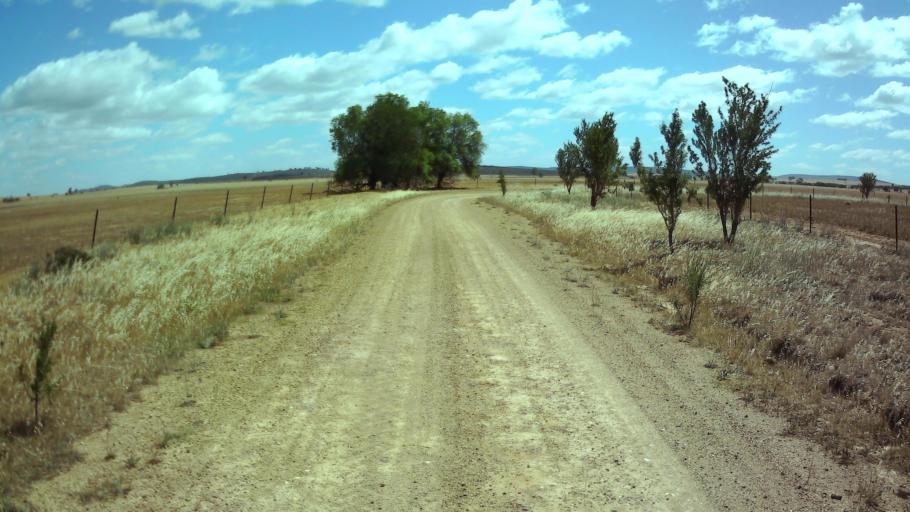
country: AU
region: New South Wales
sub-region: Weddin
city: Grenfell
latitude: -33.9893
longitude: 148.3151
